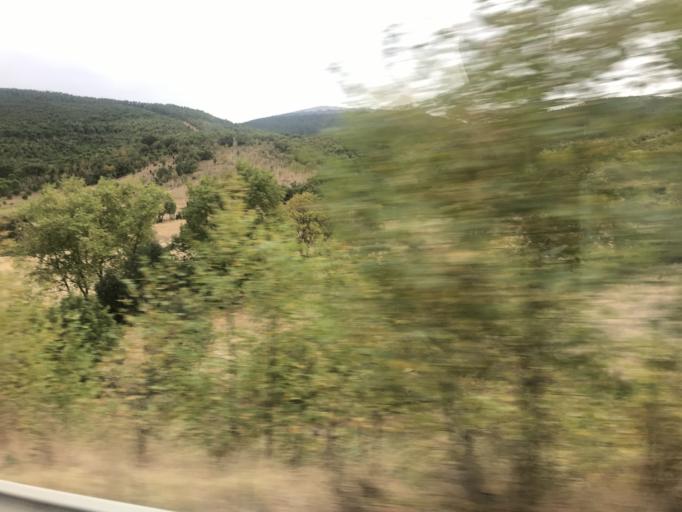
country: TR
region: Balikesir
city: Ergama
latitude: 39.6270
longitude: 27.6018
